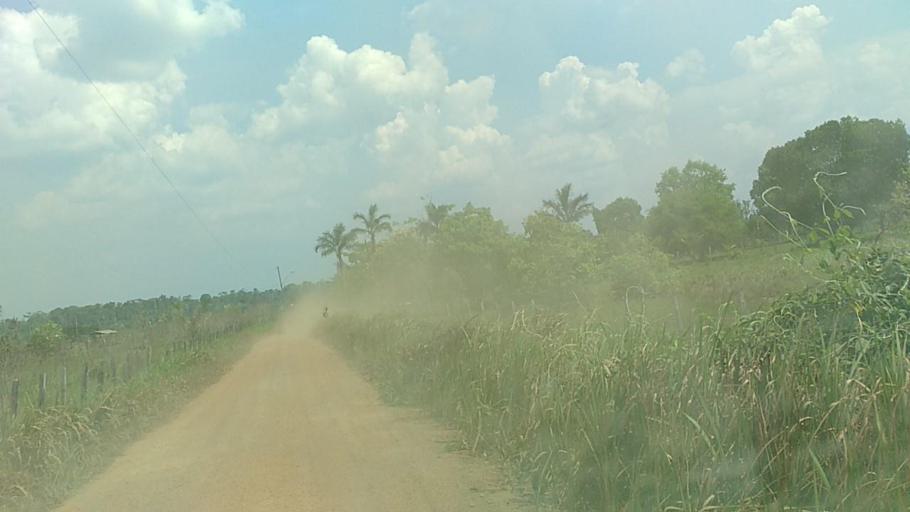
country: BR
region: Rondonia
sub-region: Porto Velho
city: Porto Velho
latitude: -8.6536
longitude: -64.1668
